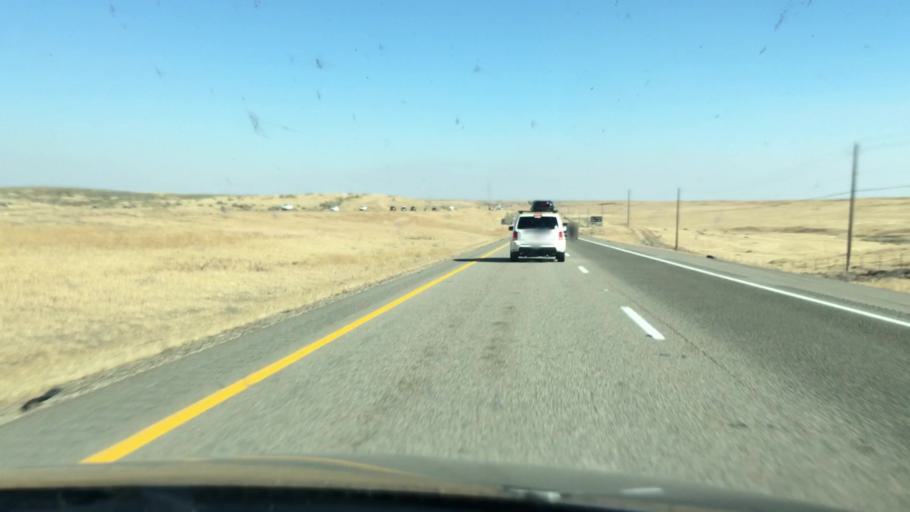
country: US
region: Idaho
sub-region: Ada County
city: Boise
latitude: 43.4499
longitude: -116.0782
